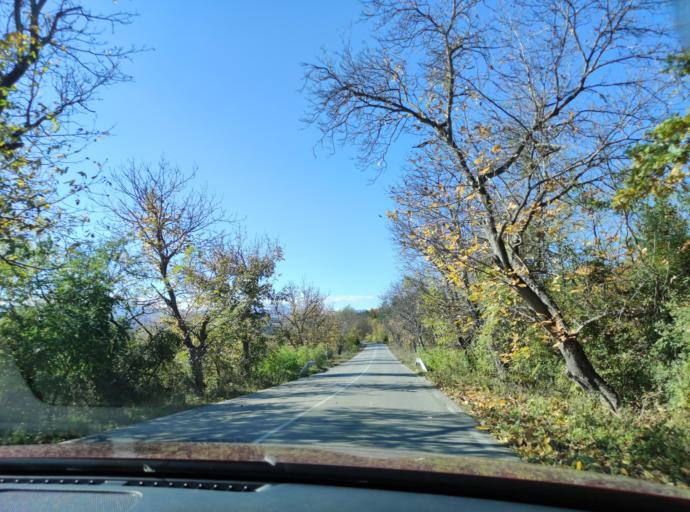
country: BG
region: Montana
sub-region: Obshtina Montana
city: Montana
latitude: 43.4047
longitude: 23.0747
